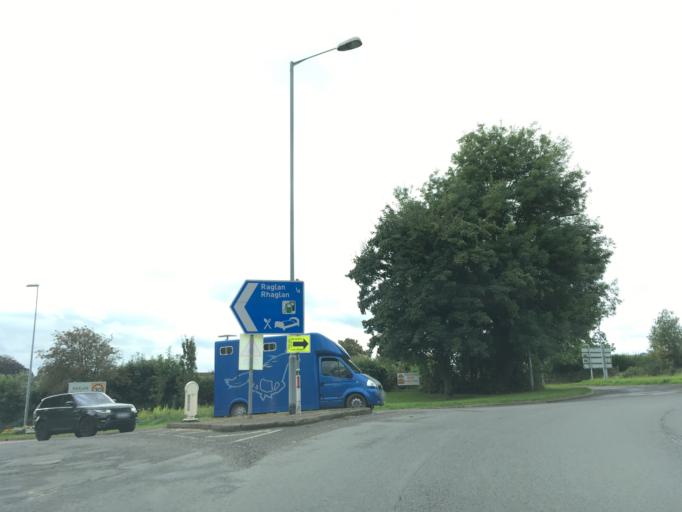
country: GB
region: Wales
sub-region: Monmouthshire
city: Llanarth
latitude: 51.7661
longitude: -2.8559
